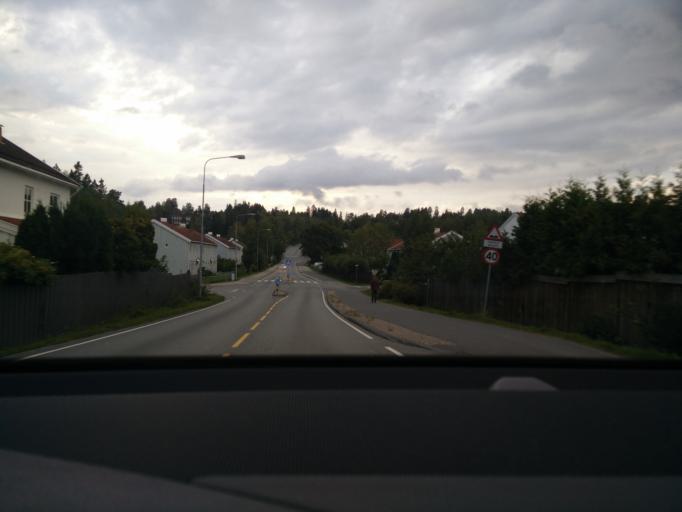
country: NO
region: Akershus
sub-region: Baerum
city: Lysaker
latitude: 59.9349
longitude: 10.6111
